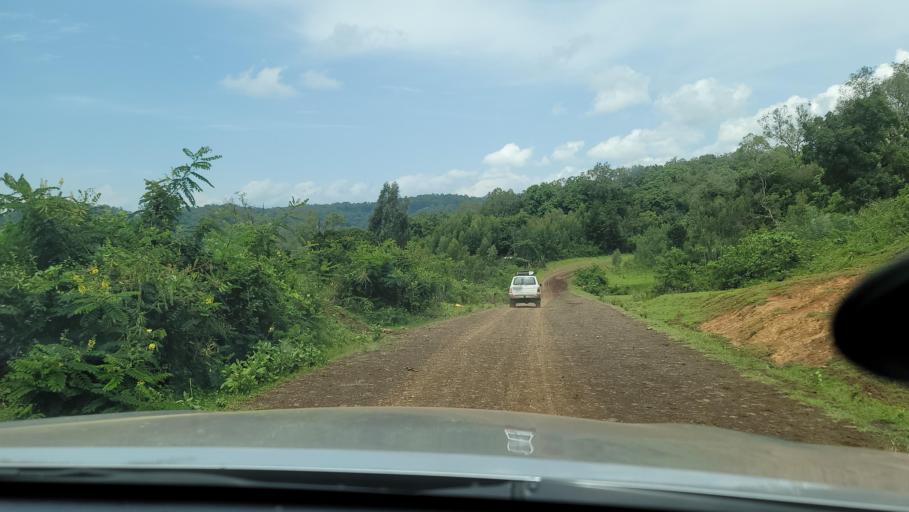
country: ET
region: Southern Nations, Nationalities, and People's Region
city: Bonga
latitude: 7.6975
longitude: 36.2469
